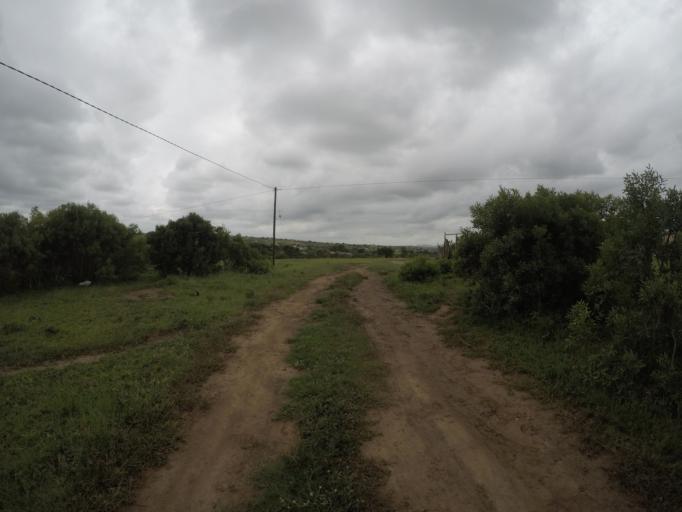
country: ZA
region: KwaZulu-Natal
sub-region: uThungulu District Municipality
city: Empangeni
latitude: -28.5914
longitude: 31.8438
